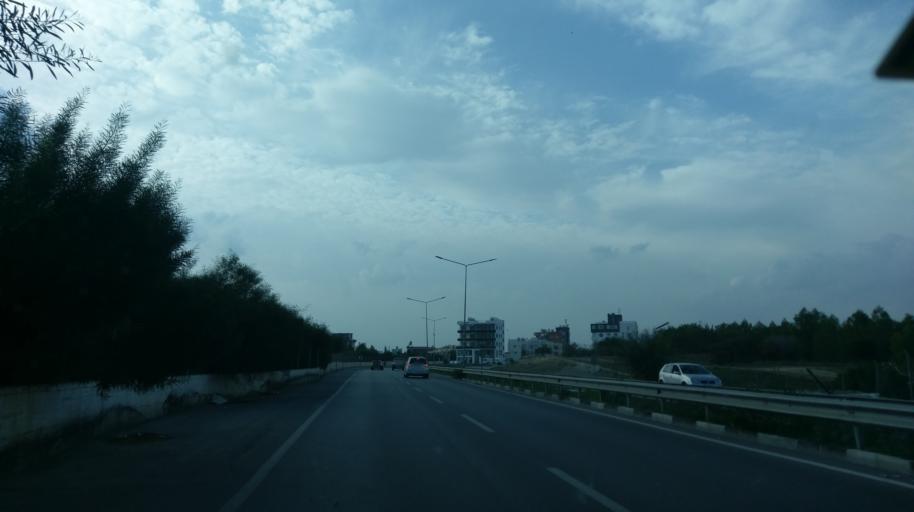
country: CY
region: Lefkosia
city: Nicosia
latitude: 35.1900
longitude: 33.3298
